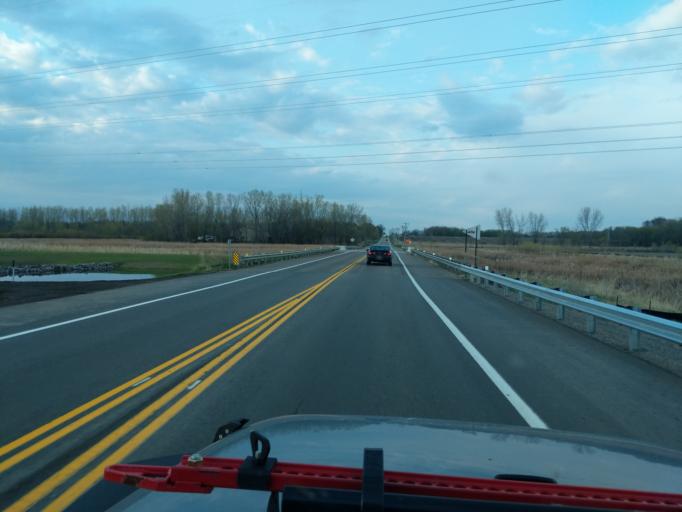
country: US
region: Minnesota
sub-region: Hennepin County
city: Rogers
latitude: 45.1554
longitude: -93.5218
